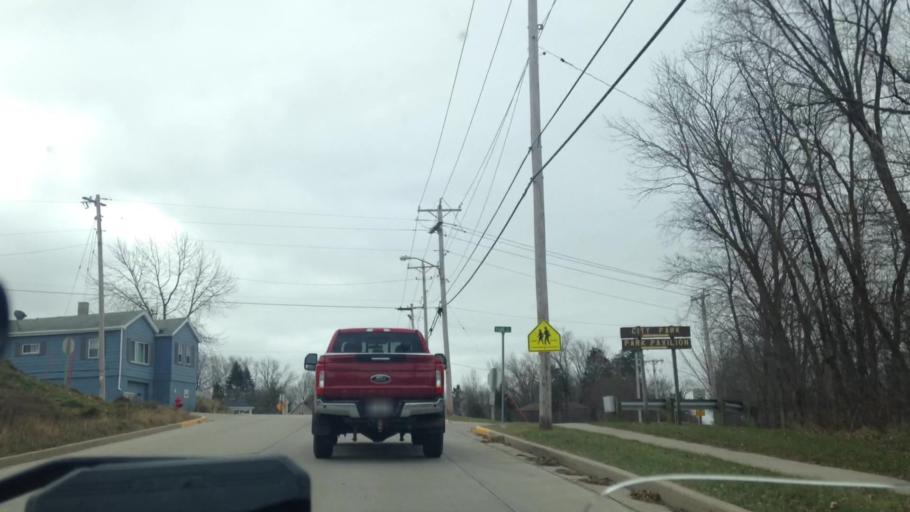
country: US
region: Wisconsin
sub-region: Dodge County
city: Mayville
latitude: 43.4943
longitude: -88.5416
